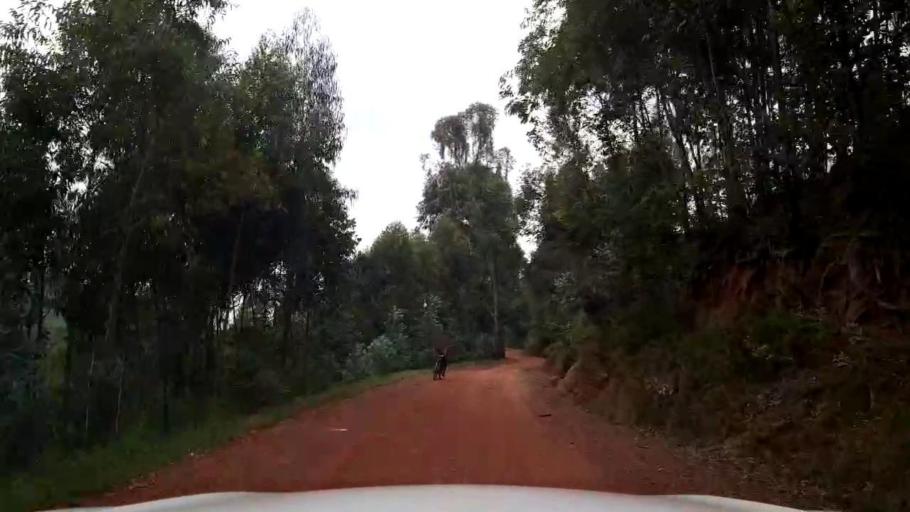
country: RW
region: Northern Province
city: Byumba
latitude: -1.5233
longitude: 29.9525
